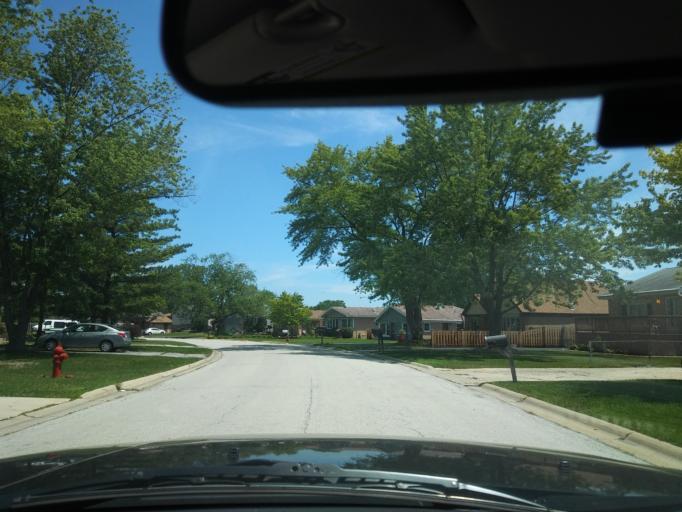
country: US
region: Illinois
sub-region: Cook County
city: Oak Forest
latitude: 41.5963
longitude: -87.7534
